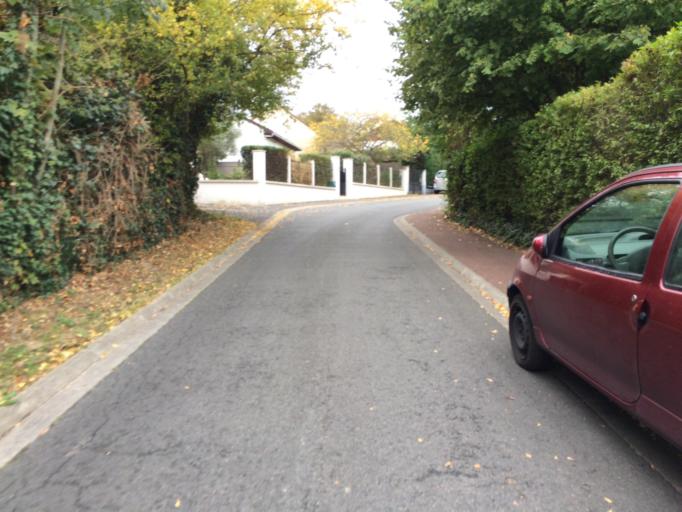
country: FR
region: Ile-de-France
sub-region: Departement de l'Essonne
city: Villebon-sur-Yvette
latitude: 48.7026
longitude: 2.2475
